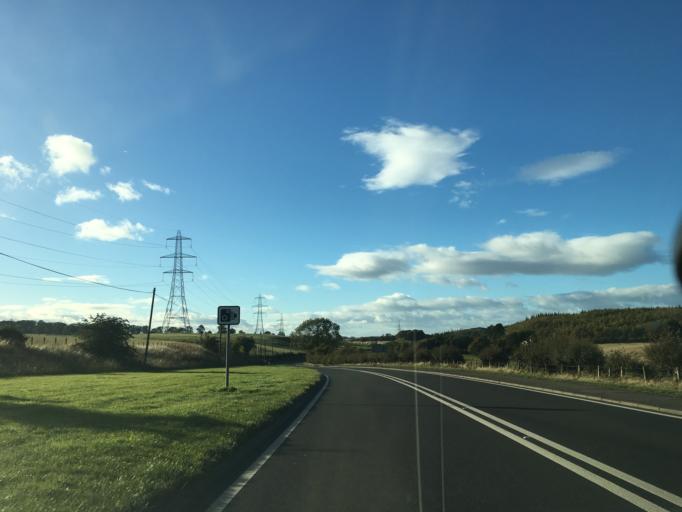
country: GB
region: Scotland
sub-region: Fife
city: Pathhead
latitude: 55.8449
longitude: -2.9259
